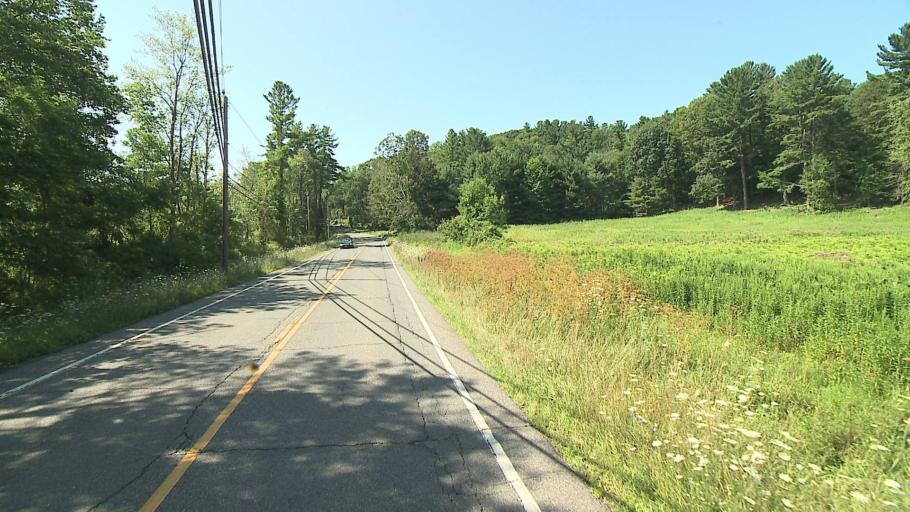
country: US
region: Connecticut
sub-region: Litchfield County
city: Canaan
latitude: 41.9981
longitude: -73.4251
